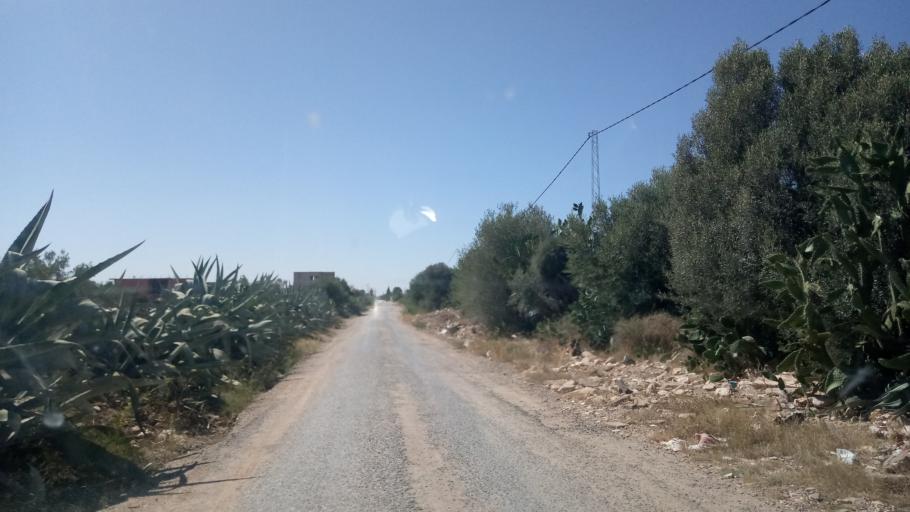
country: TN
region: Al Qayrawan
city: Sbikha
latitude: 36.1278
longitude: 10.0849
